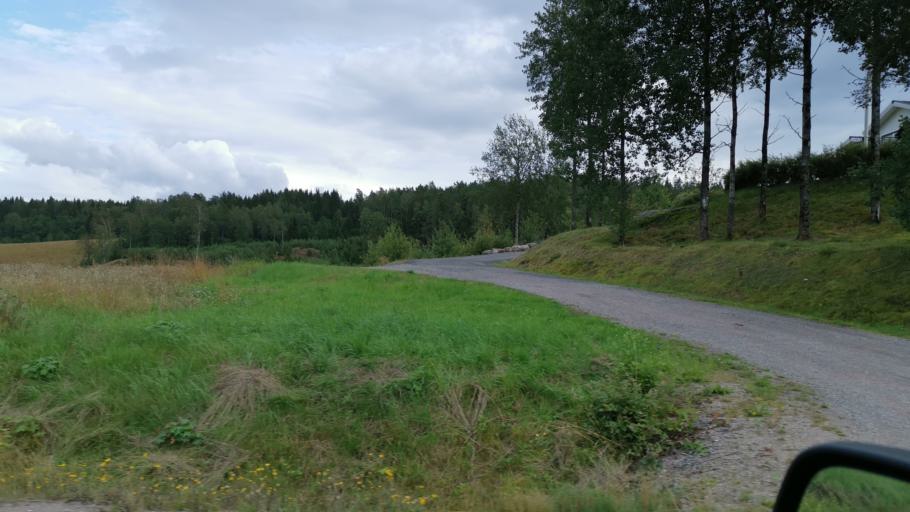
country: SE
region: Vaestra Goetaland
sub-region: Munkedals Kommun
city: Munkedal
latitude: 58.3893
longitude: 11.7484
